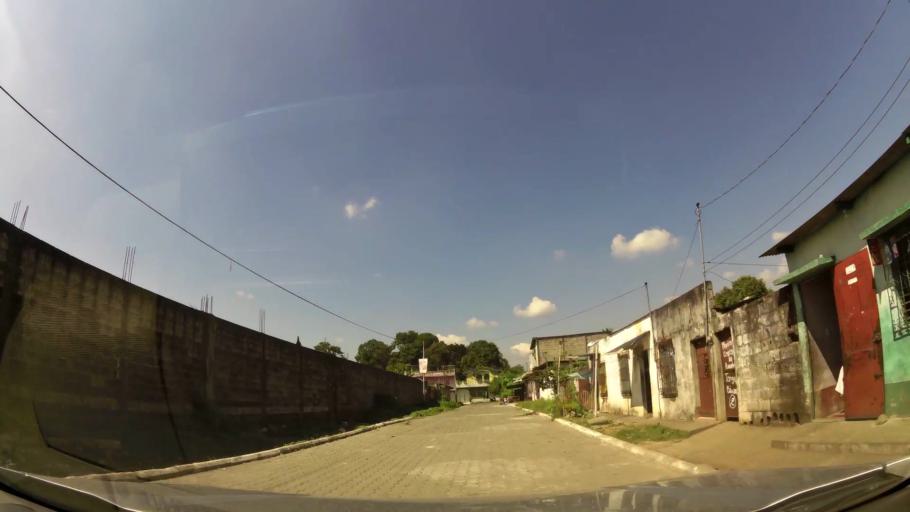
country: GT
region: Suchitepeque
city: Mazatenango
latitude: 14.5339
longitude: -91.4968
